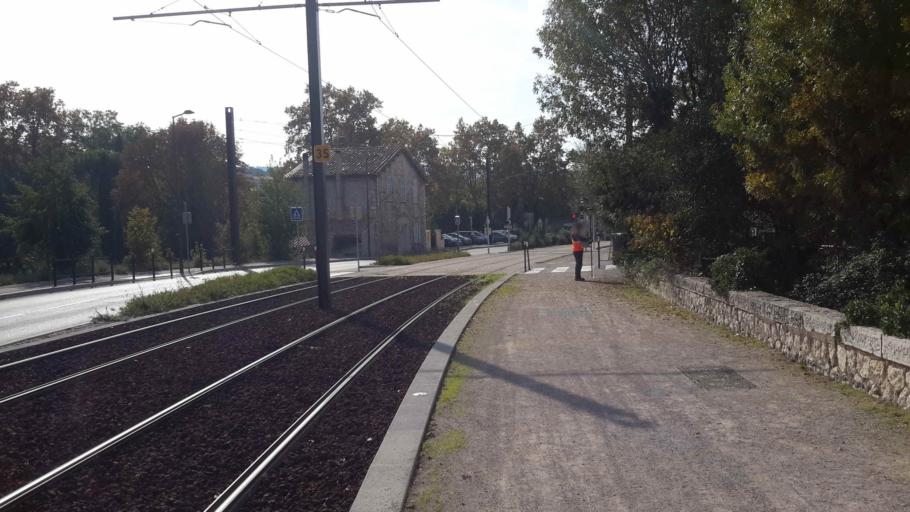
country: FR
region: Provence-Alpes-Cote d'Azur
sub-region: Departement des Bouches-du-Rhone
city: Aubagne
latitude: 43.2869
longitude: 5.5560
